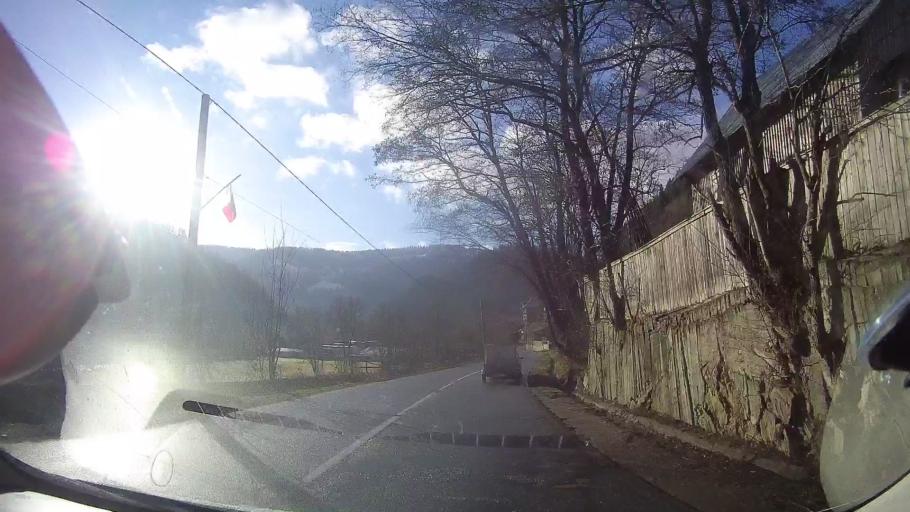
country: RO
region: Alba
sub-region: Comuna Vadu Motilor
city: Vadu Motilor
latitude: 46.4040
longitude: 22.9636
